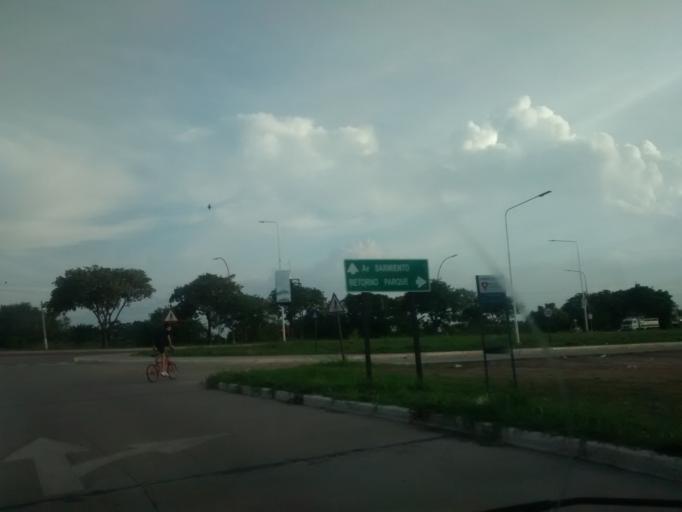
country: AR
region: Chaco
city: Resistencia
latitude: -27.4326
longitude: -58.9667
